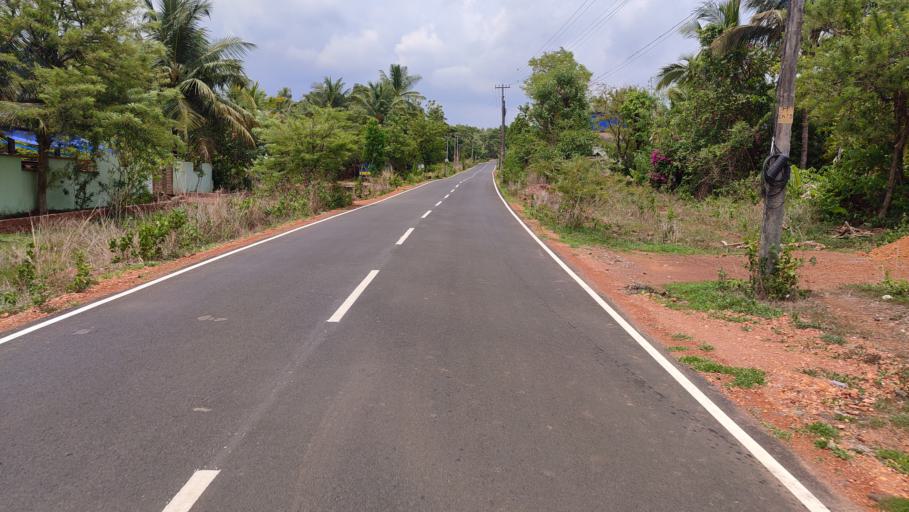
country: IN
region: Kerala
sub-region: Kasaragod District
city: Kannangad
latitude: 12.3220
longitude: 75.1248
